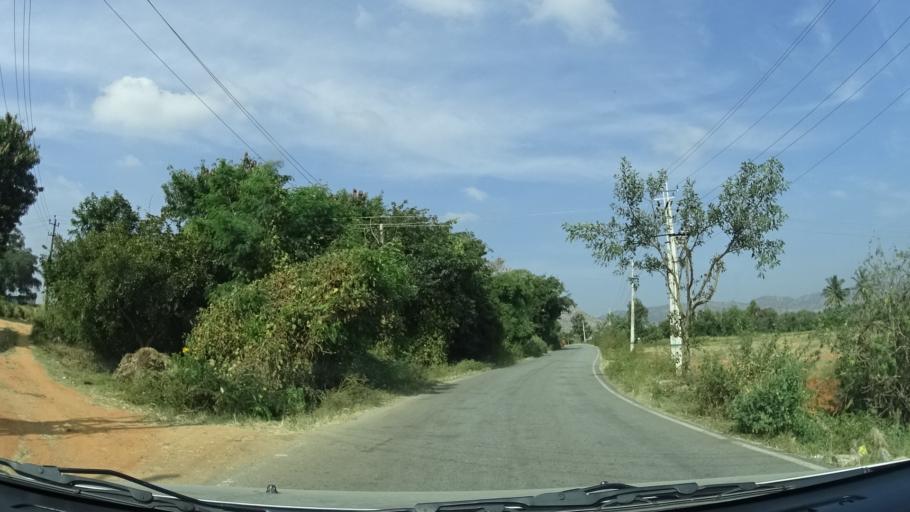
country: IN
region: Karnataka
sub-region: Chikkaballapur
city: Chik Ballapur
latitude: 13.4051
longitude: 77.7186
